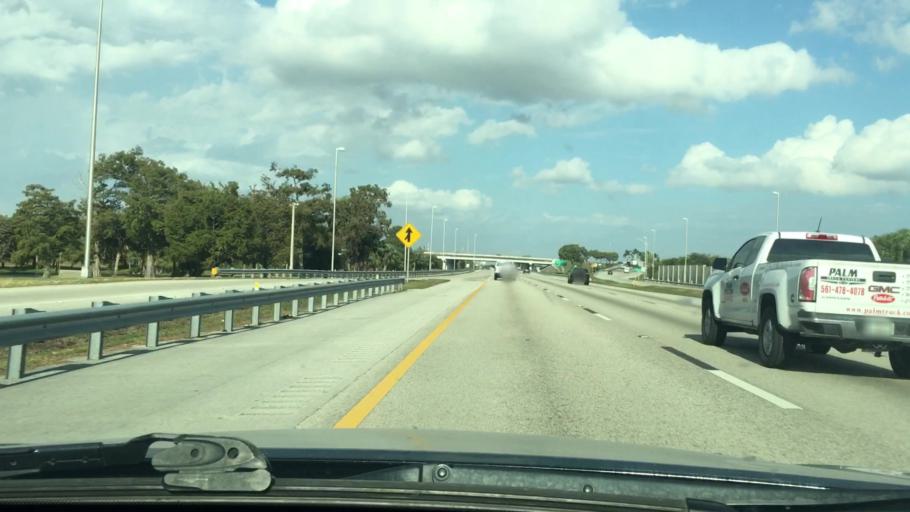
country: US
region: Florida
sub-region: Broward County
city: Coconut Creek
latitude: 26.2276
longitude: -80.1802
